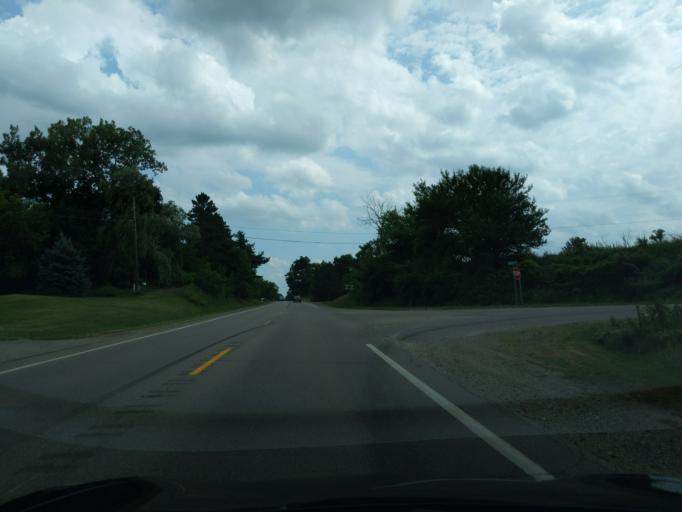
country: US
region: Michigan
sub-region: Eaton County
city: Eaton Rapids
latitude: 42.4835
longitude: -84.6598
